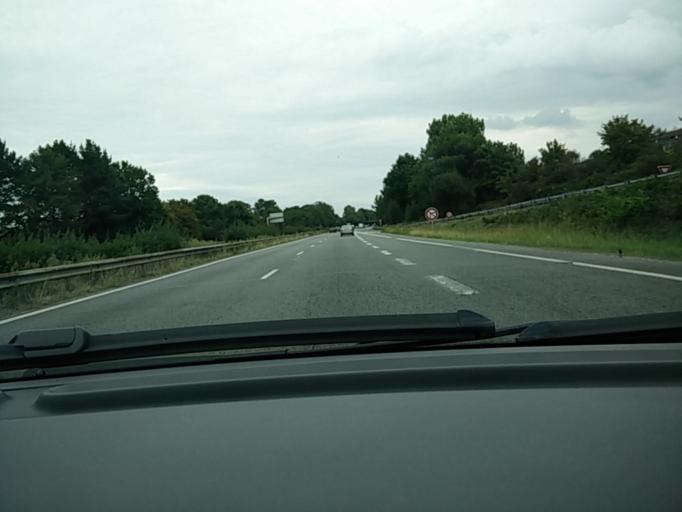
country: FR
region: Aquitaine
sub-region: Departement de la Gironde
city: Le Haillan
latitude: 44.8584
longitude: -0.6614
